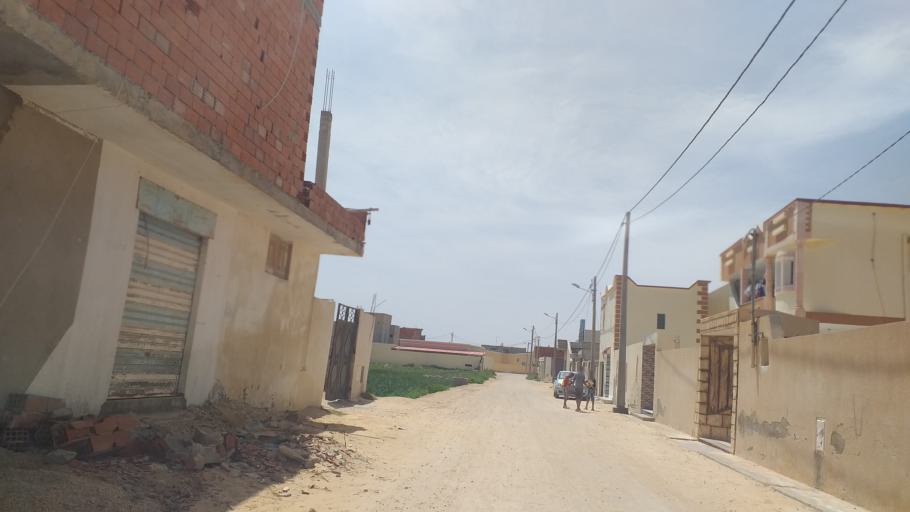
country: TN
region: Qabis
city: Gabes
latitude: 33.9508
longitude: 10.0638
